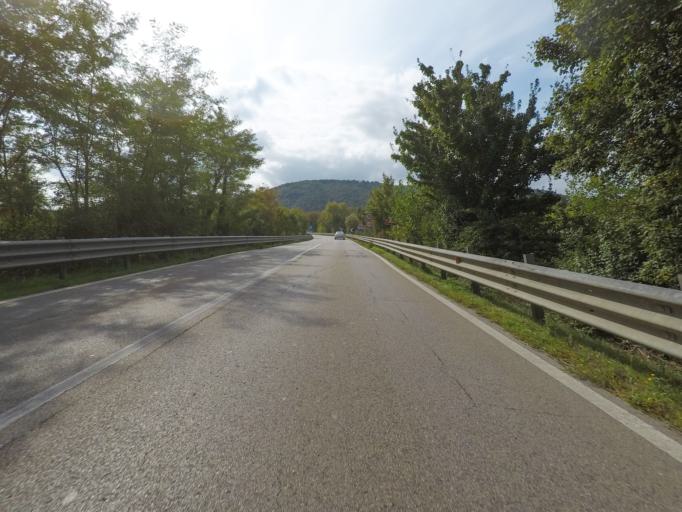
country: IT
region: Tuscany
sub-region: Provincia di Siena
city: Murlo
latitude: 43.1493
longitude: 11.2867
